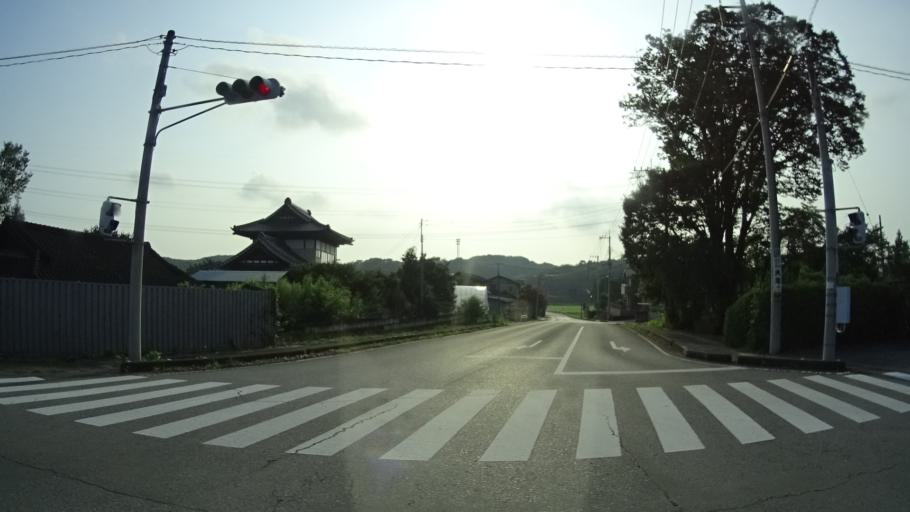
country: JP
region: Tochigi
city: Motegi
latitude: 36.5628
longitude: 140.1030
